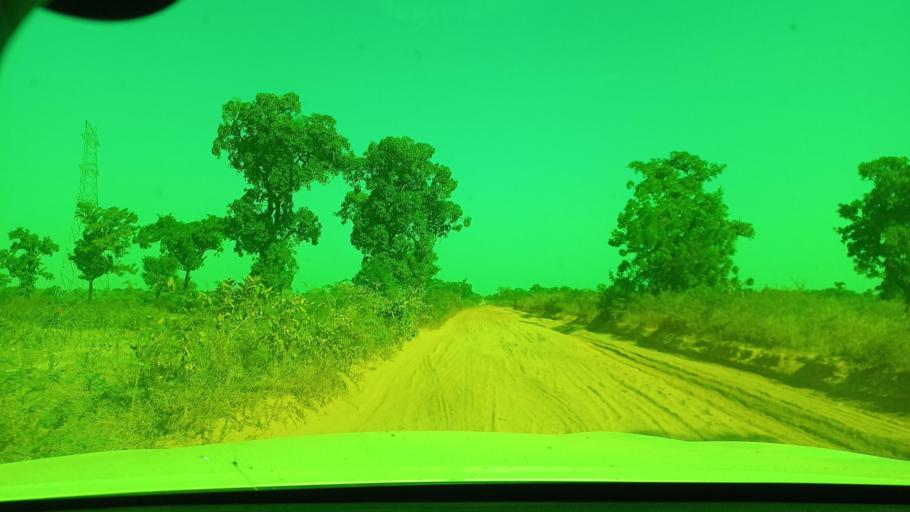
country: ML
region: Bamako
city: Bamako
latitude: 12.3976
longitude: -7.9950
